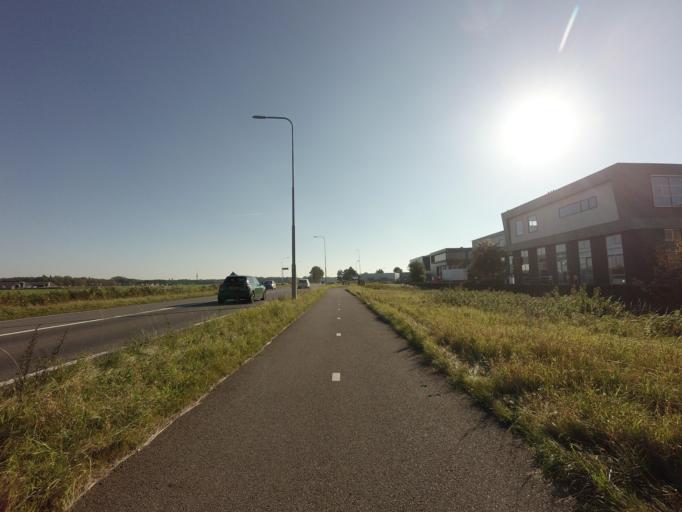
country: NL
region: North Holland
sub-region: Gemeente Wijdemeren
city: Kortenhoef
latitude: 52.2706
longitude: 5.1205
